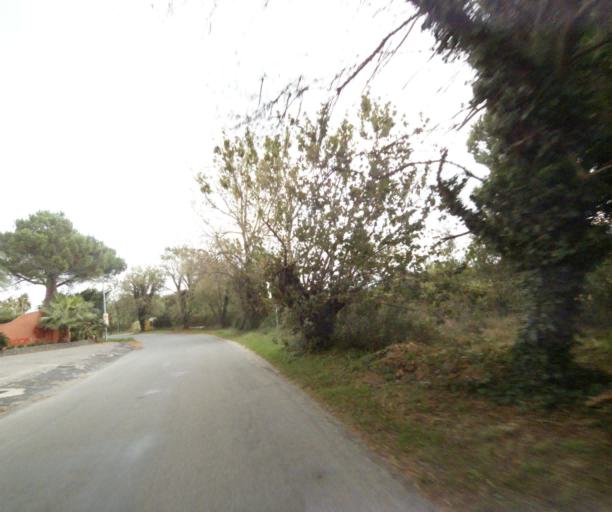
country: FR
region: Languedoc-Roussillon
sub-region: Departement des Pyrenees-Orientales
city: Argelers
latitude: 42.5679
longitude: 3.0340
